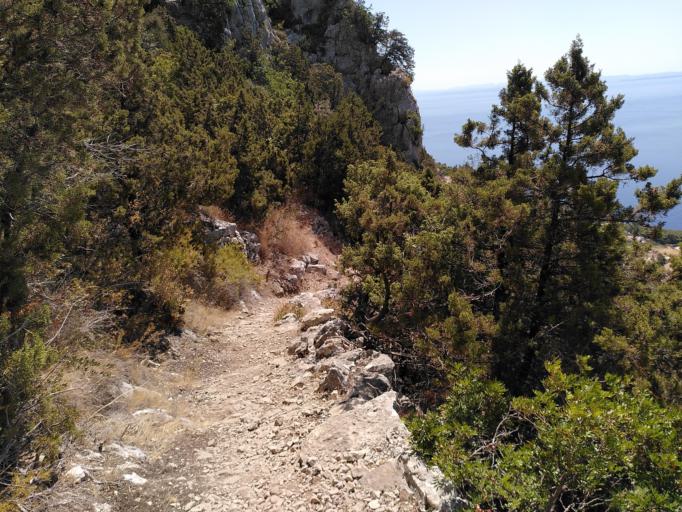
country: HR
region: Splitsko-Dalmatinska
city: Stari Grad
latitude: 43.1438
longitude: 16.5884
